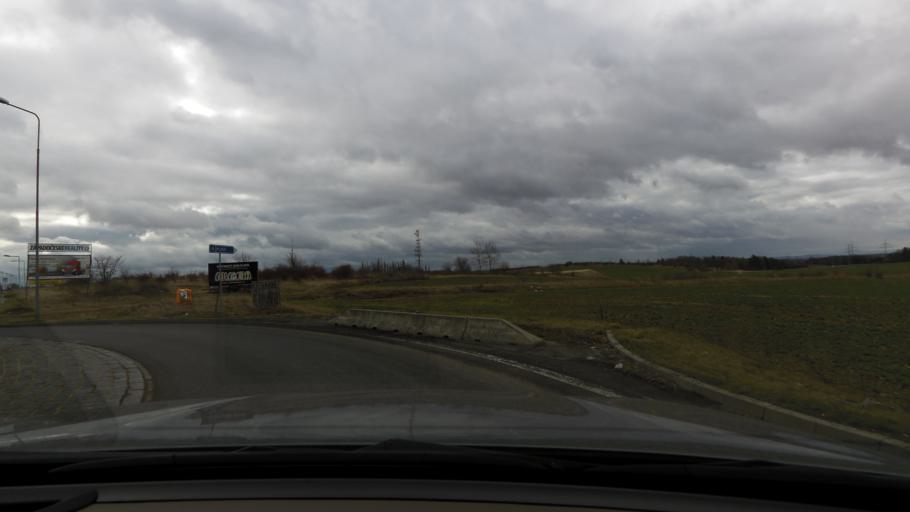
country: CZ
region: Plzensky
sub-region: Okres Plzen-Mesto
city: Pilsen
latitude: 49.7758
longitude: 13.3469
